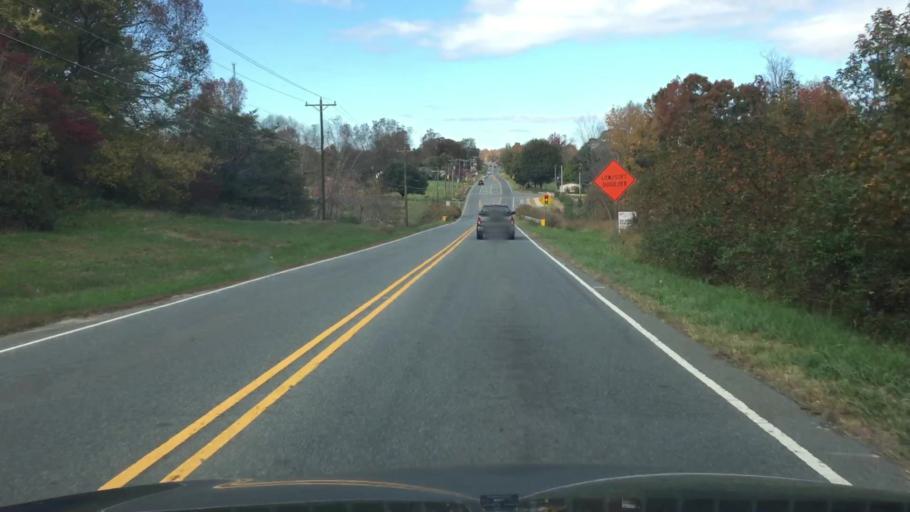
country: US
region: North Carolina
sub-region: Iredell County
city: Troutman
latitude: 35.6616
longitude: -80.8497
